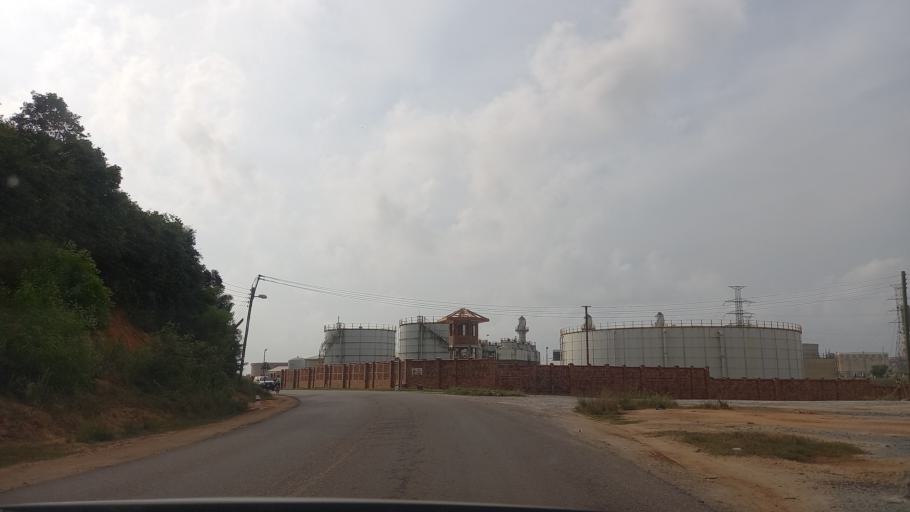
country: GH
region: Western
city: Shama Junction
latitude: 4.9767
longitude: -1.6587
